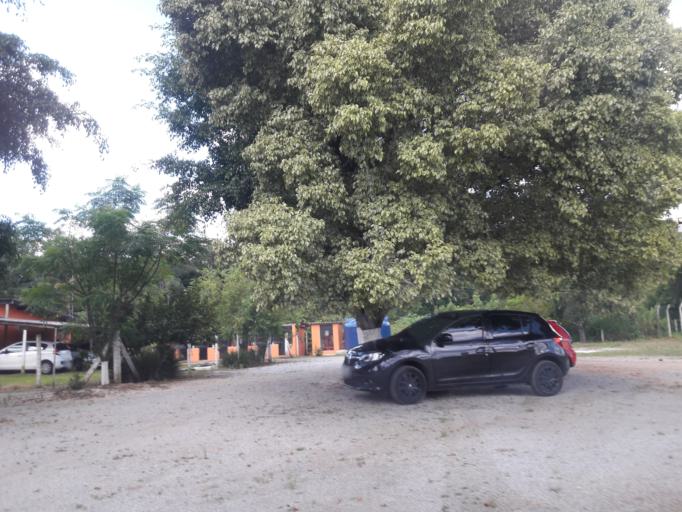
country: BR
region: Sao Paulo
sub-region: Campo Limpo Paulista
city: Campo Limpo Paulista
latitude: -23.2052
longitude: -46.7936
